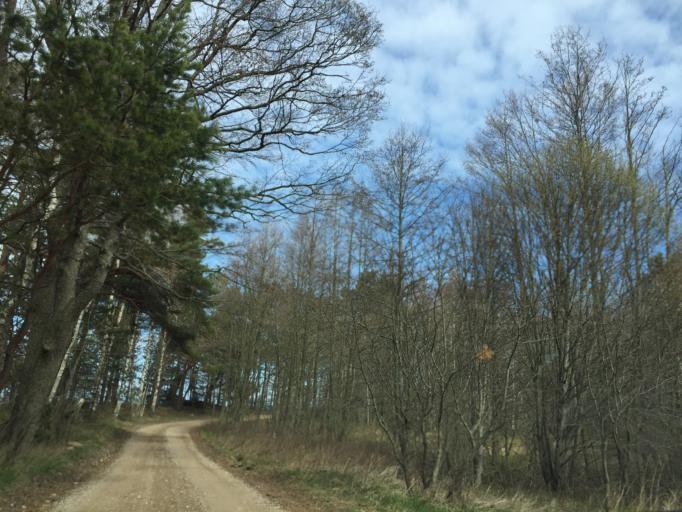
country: LV
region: Salacgrivas
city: Salacgriva
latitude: 57.5995
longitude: 24.3734
